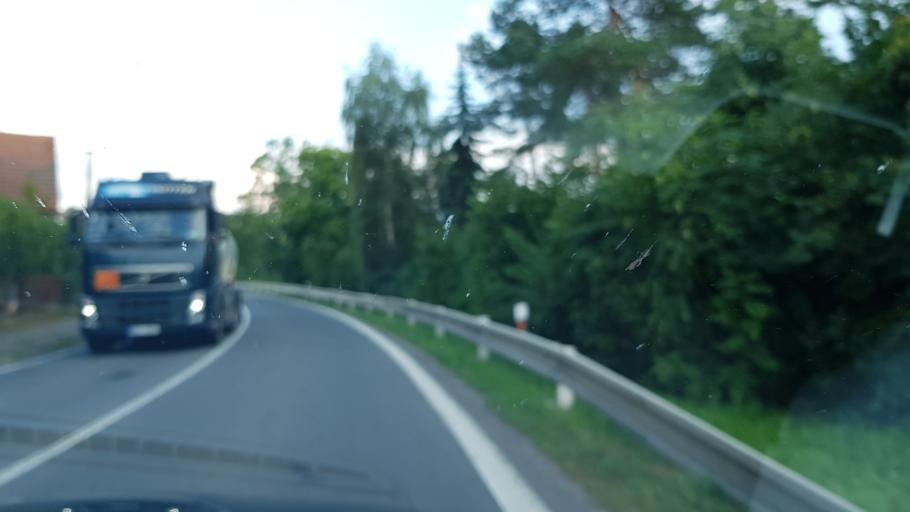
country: CZ
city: Doudleby nad Orlici
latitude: 50.1112
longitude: 16.2538
